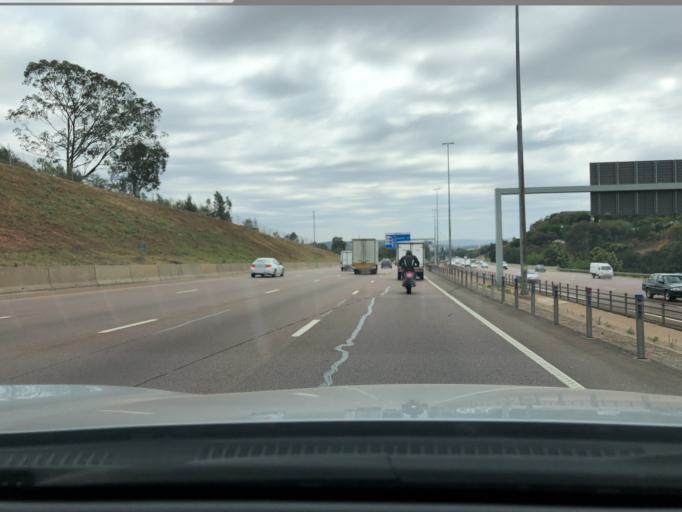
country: ZA
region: Gauteng
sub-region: City of Tshwane Metropolitan Municipality
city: Pretoria
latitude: -25.8012
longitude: 28.2617
